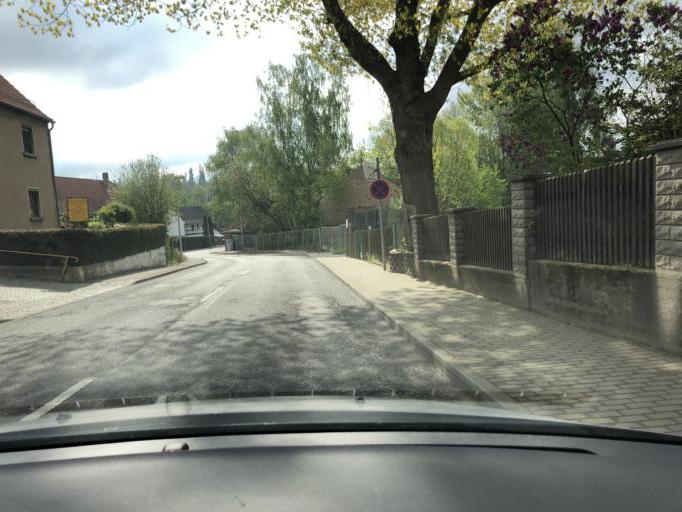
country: DE
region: Thuringia
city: Altenburg
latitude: 51.0075
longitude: 12.4397
